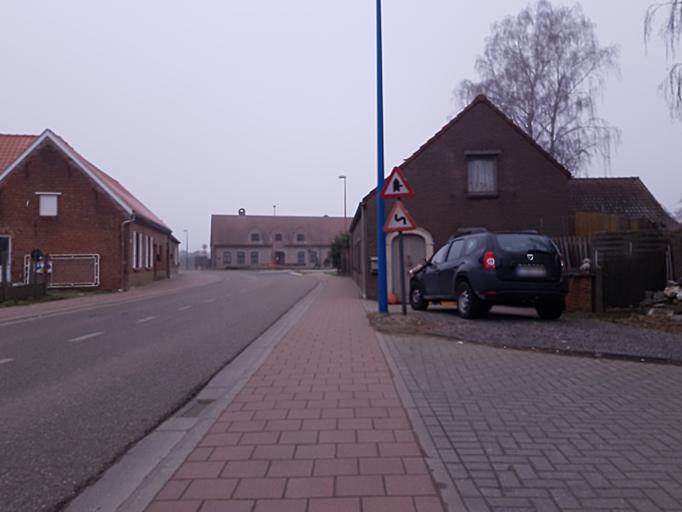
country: BE
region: Flanders
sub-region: Provincie Vlaams-Brabant
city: Grimbergen
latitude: 50.9491
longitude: 4.3964
